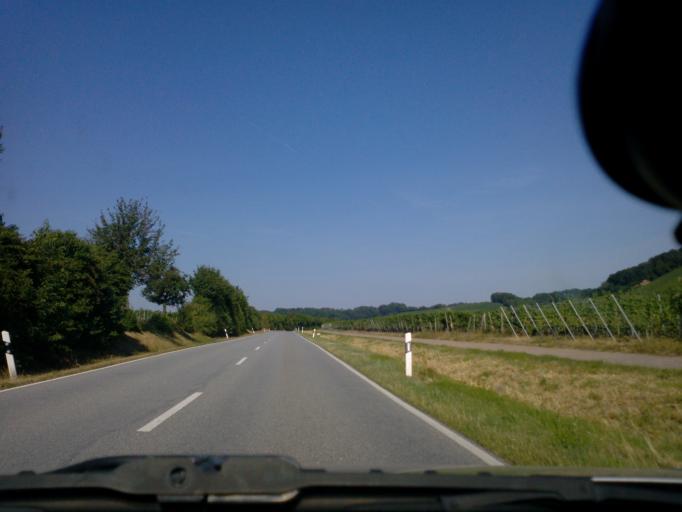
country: DE
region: Baden-Wuerttemberg
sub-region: Regierungsbezirk Stuttgart
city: Brackenheim
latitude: 49.0968
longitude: 9.0358
